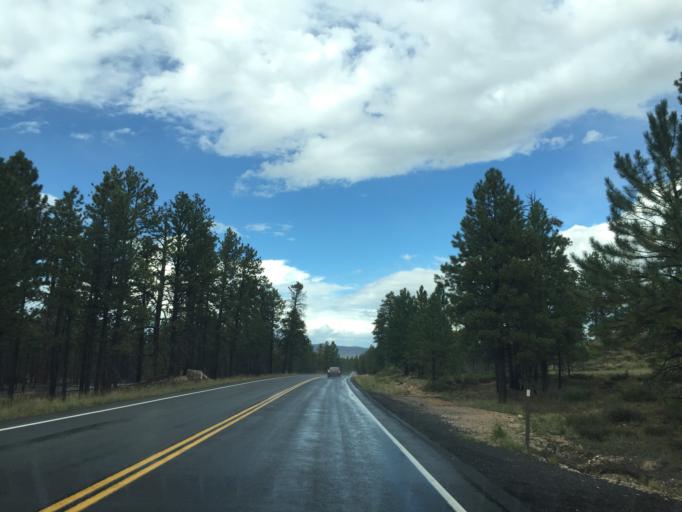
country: US
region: Utah
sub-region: Garfield County
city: Panguitch
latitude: 37.6488
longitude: -112.1649
